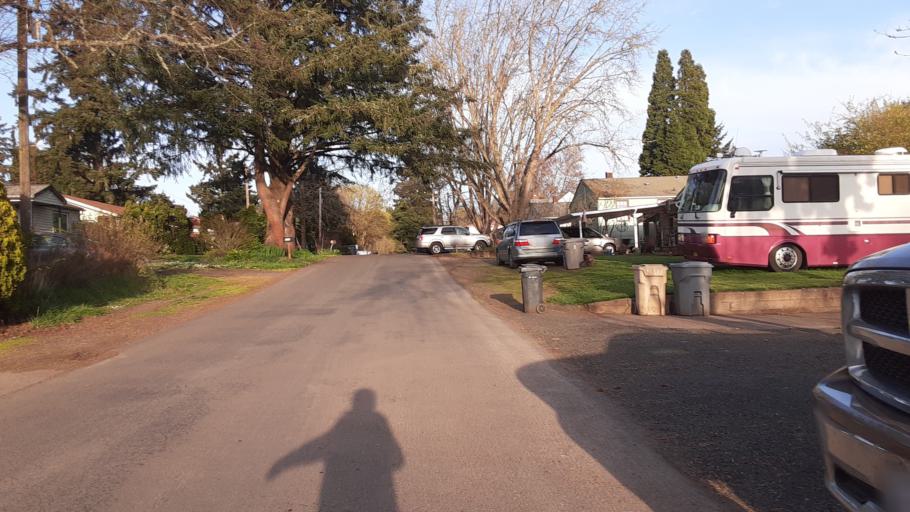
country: US
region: Oregon
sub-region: Benton County
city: Corvallis
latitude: 44.5502
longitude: -123.2627
